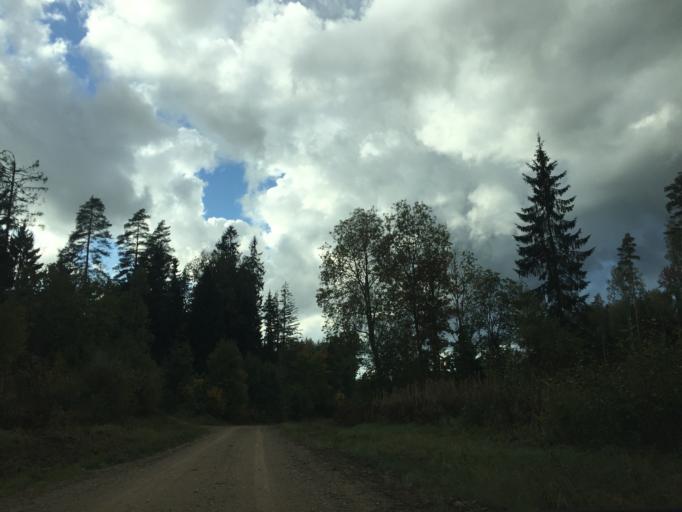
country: LV
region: Ligatne
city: Ligatne
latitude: 57.1027
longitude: 25.1380
